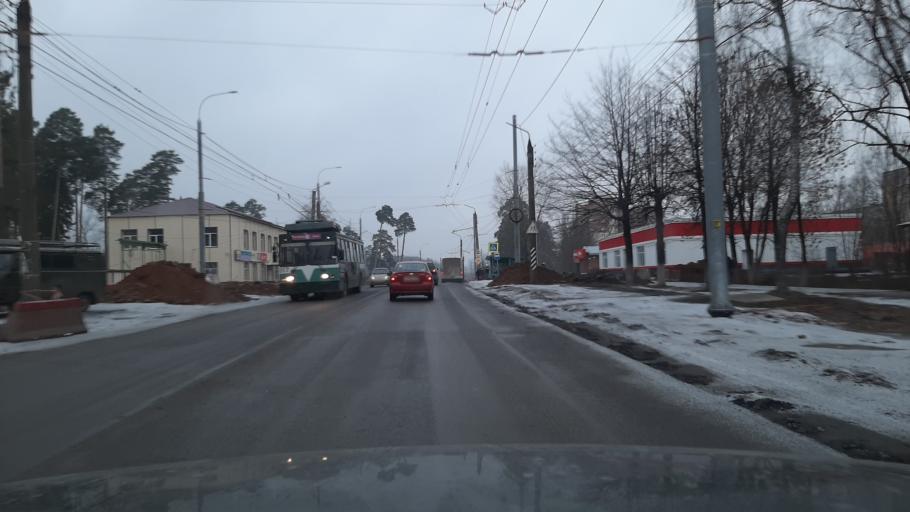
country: RU
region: Ivanovo
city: Kokhma
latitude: 56.9345
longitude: 41.0733
